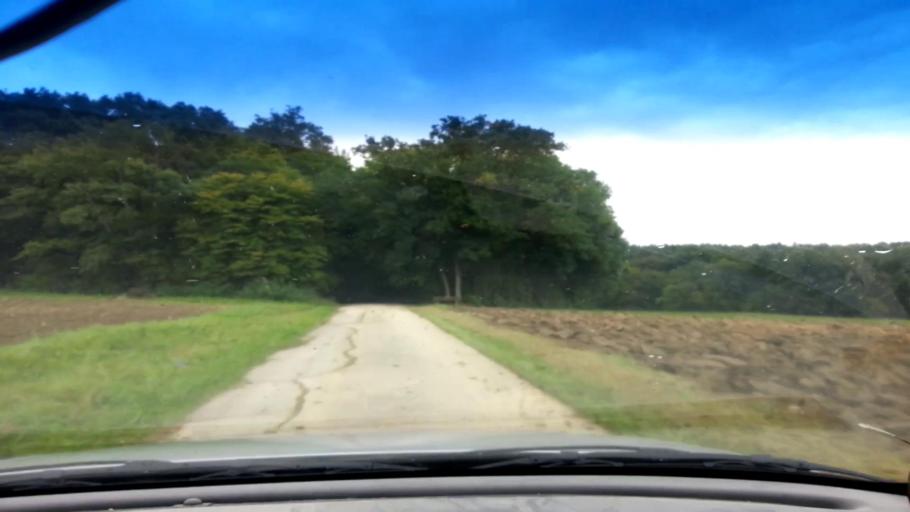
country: DE
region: Bavaria
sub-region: Upper Franconia
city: Litzendorf
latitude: 49.9367
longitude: 11.0012
